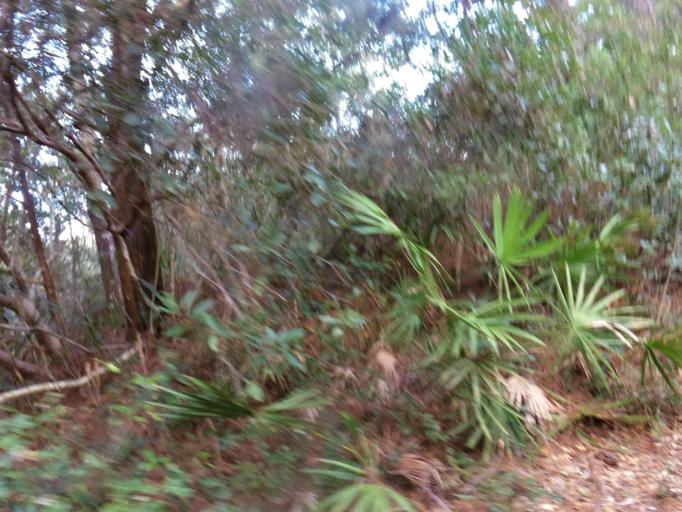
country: US
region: Florida
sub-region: Duval County
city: Atlantic Beach
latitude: 30.4633
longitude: -81.4196
